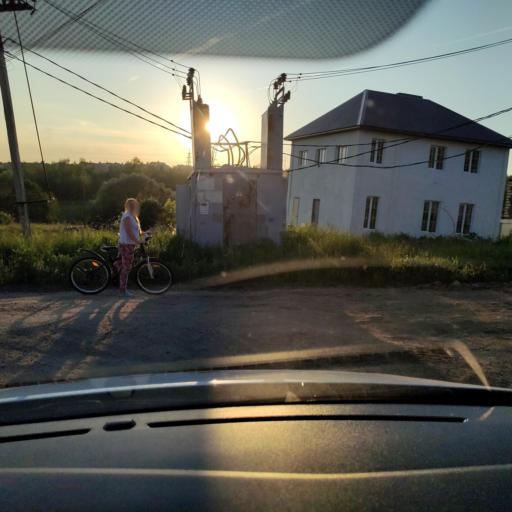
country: RU
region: Tatarstan
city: Stolbishchi
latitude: 55.7527
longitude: 49.3010
